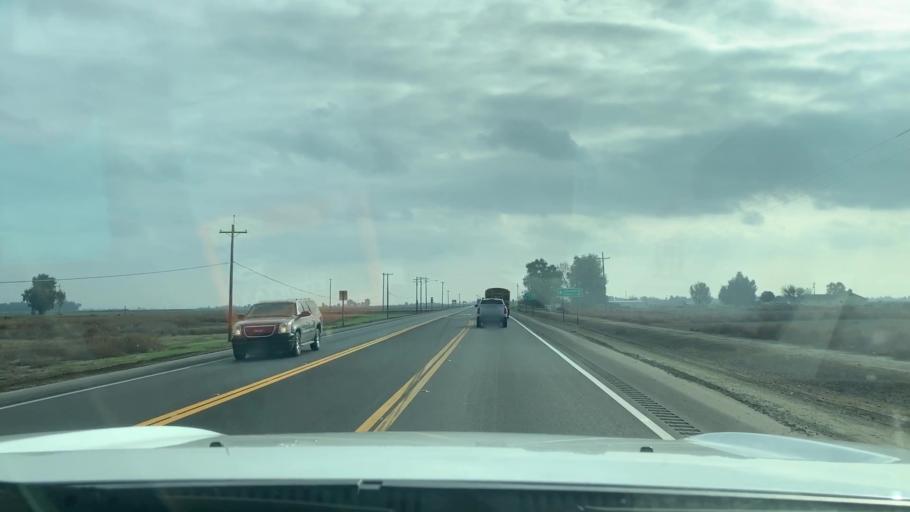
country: US
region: California
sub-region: Kings County
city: Stratford
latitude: 36.2139
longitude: -119.8162
